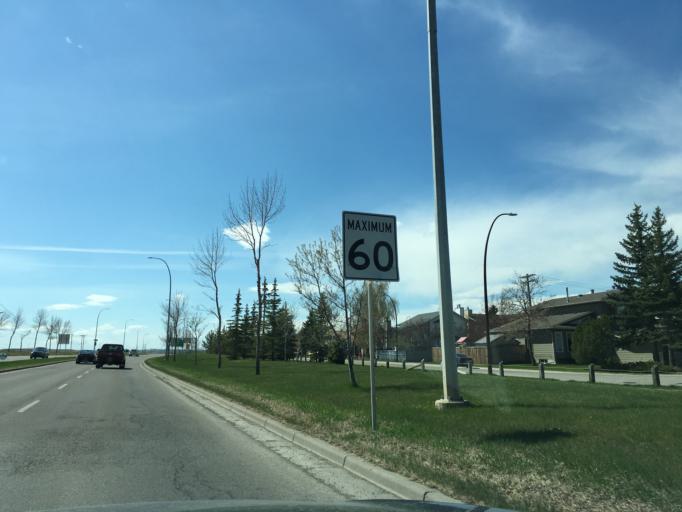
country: CA
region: Alberta
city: Calgary
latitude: 50.9001
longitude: -114.0246
